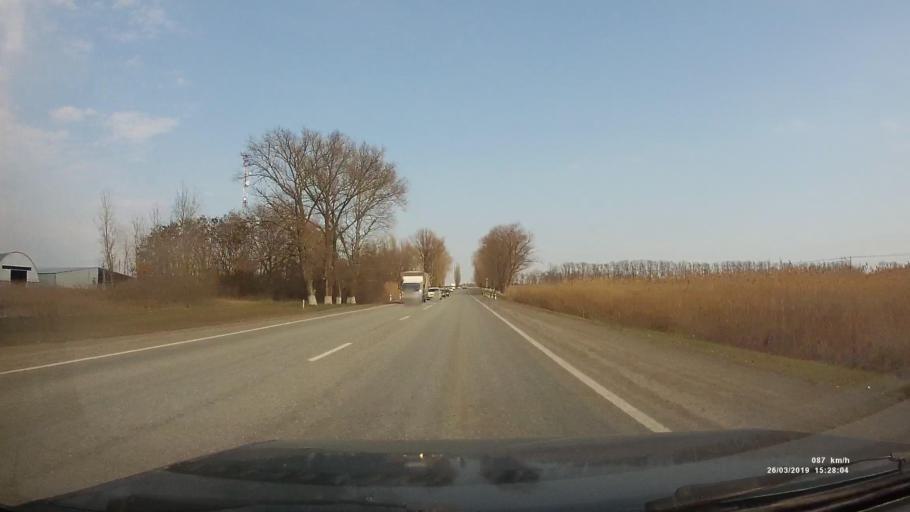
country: RU
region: Rostov
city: Primorka
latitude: 47.3219
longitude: 39.0764
